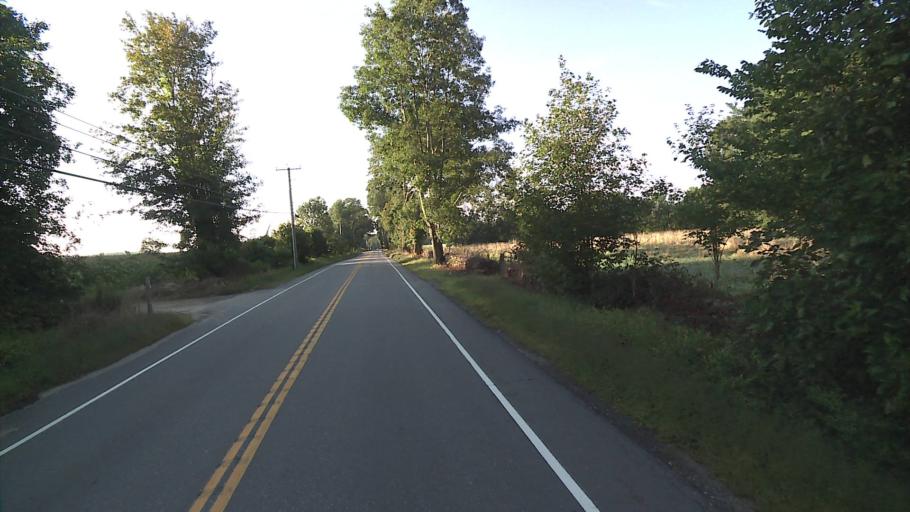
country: US
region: Connecticut
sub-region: Tolland County
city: South Coventry
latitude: 41.8124
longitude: -72.3078
